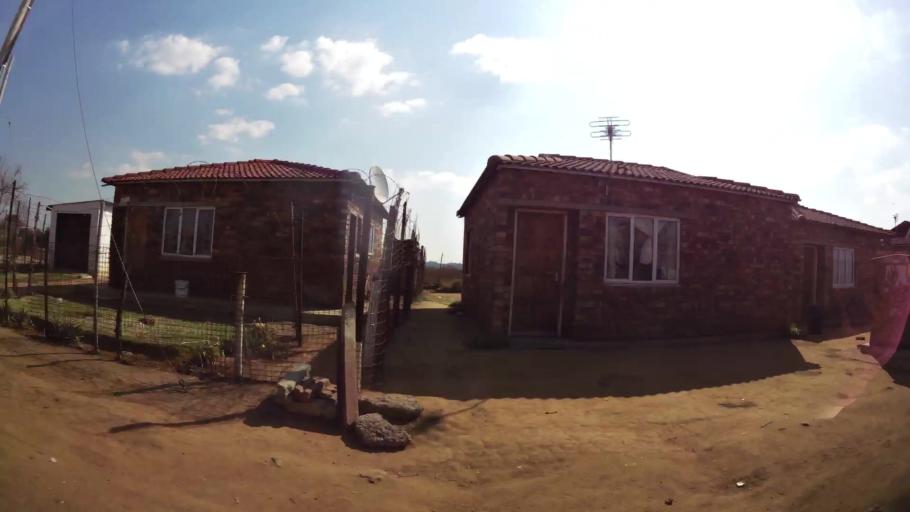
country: ZA
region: Gauteng
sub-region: Ekurhuleni Metropolitan Municipality
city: Benoni
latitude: -26.1365
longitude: 28.4088
